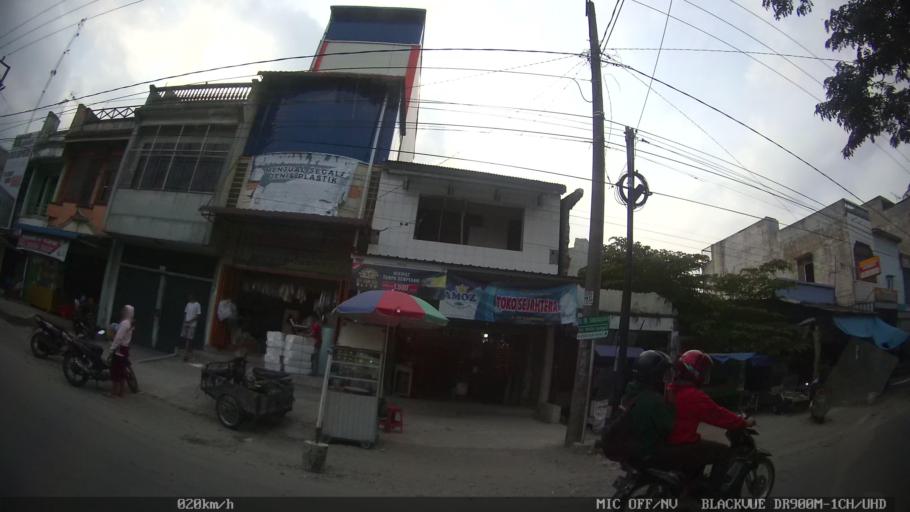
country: ID
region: North Sumatra
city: Sunggal
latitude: 3.5745
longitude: 98.6108
